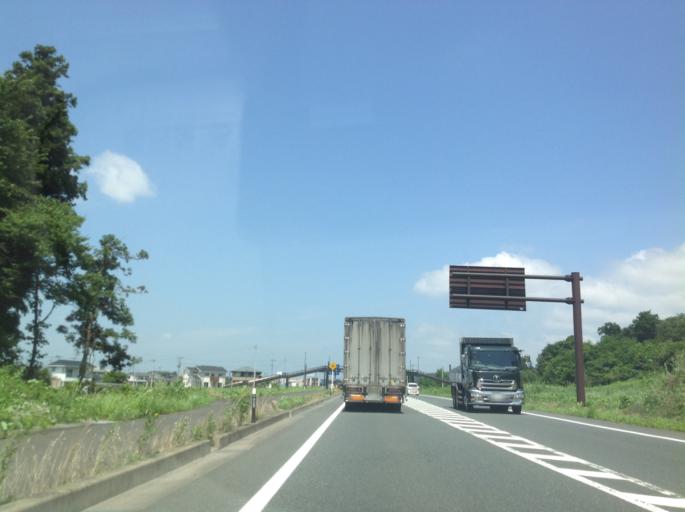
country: JP
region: Iwate
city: Hanamaki
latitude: 39.3830
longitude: 141.1426
